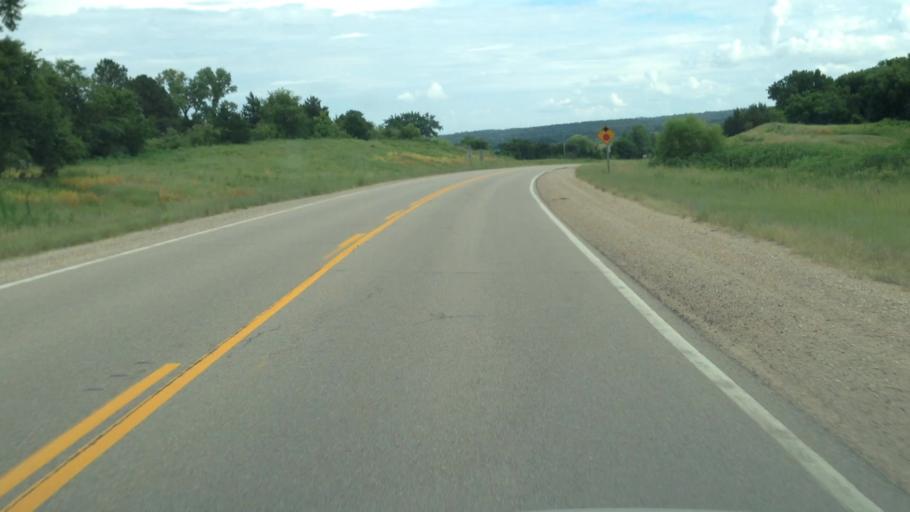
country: US
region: Kansas
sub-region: Jefferson County
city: Oskaloosa
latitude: 39.0911
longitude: -95.4743
